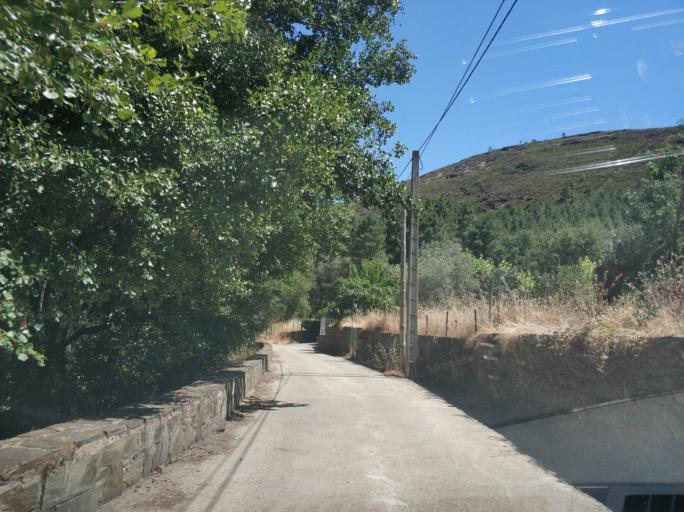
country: ES
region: Castille and Leon
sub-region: Provincia de Salamanca
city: Herguijuela de la Sierra
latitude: 40.4026
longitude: -6.0834
